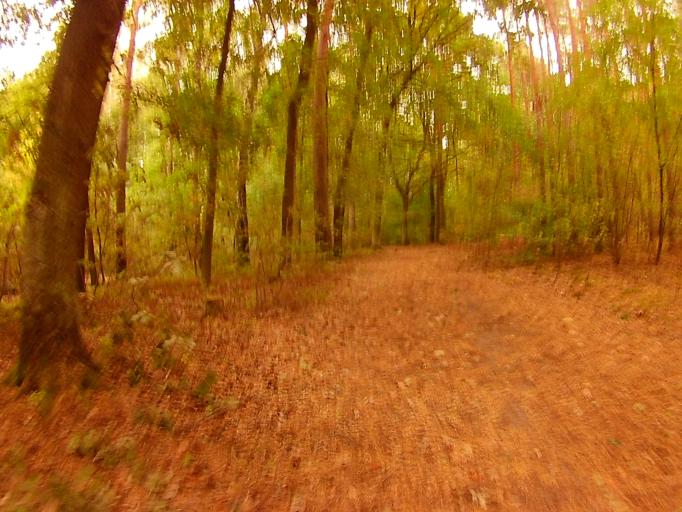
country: DE
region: Brandenburg
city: Zeuthen
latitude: 52.3929
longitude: 13.6261
